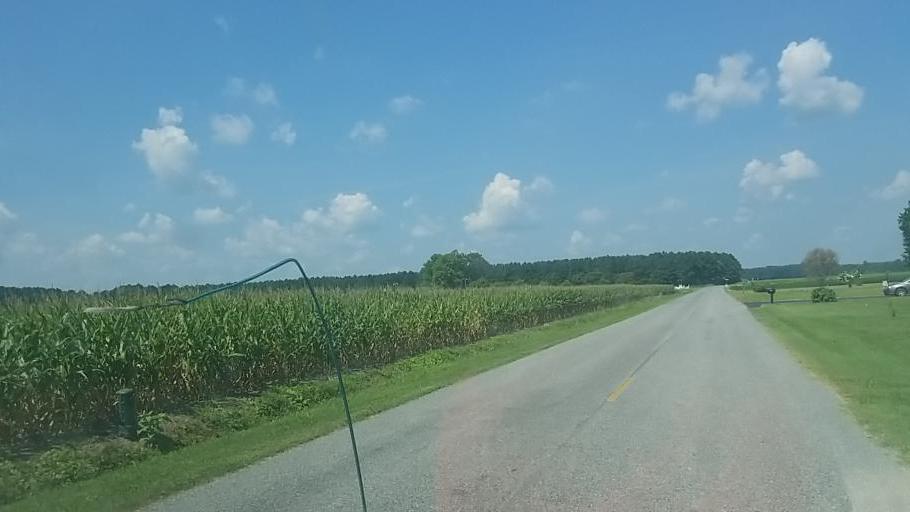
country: US
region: Maryland
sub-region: Worcester County
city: Berlin
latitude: 38.2963
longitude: -75.2629
